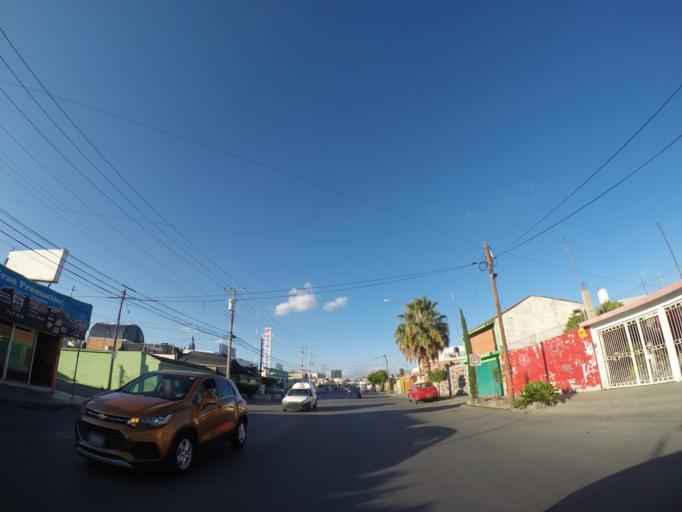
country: MX
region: San Luis Potosi
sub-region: San Luis Potosi
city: San Luis Potosi
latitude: 22.1750
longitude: -100.9984
